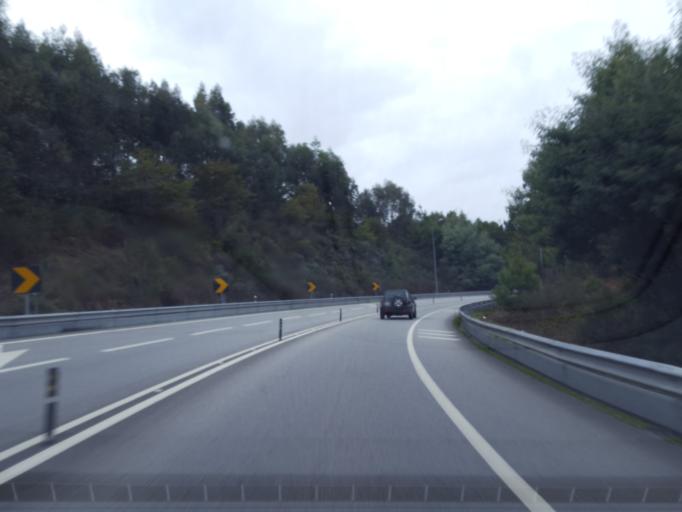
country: PT
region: Porto
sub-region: Marco de Canaveses
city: Marco de Canavezes
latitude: 41.2225
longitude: -8.1902
